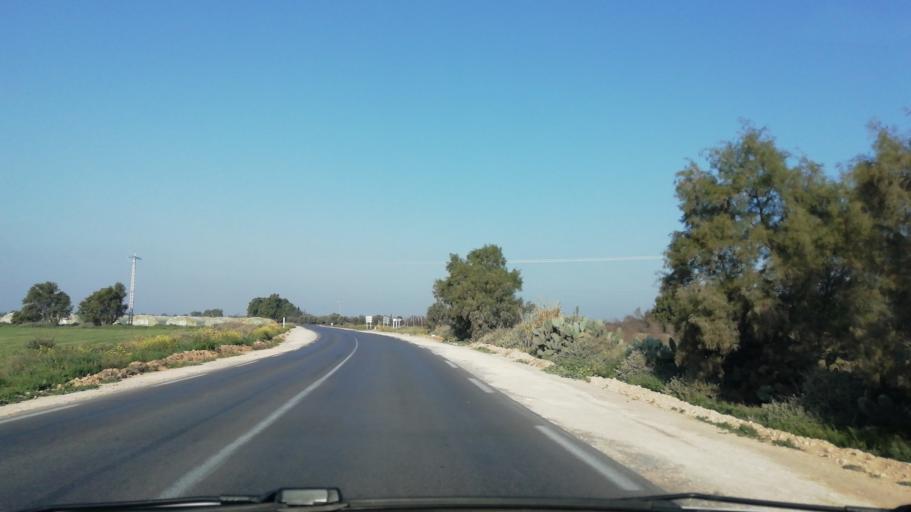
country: DZ
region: Mostaganem
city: Mostaganem
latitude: 35.7561
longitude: 0.1099
